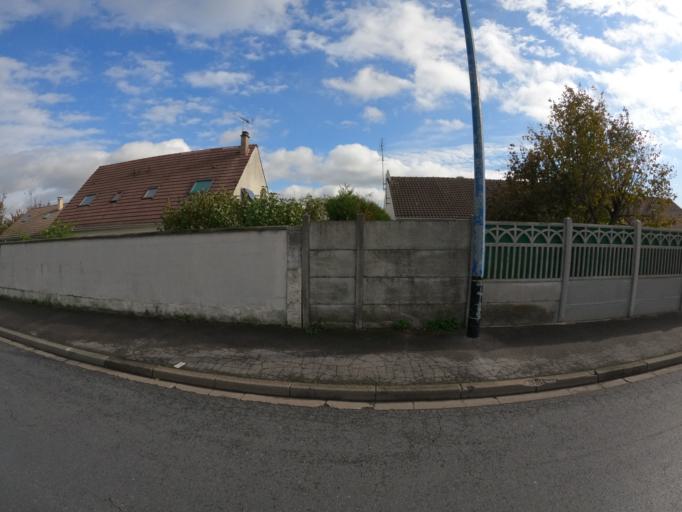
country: FR
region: Ile-de-France
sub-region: Departement de Seine-et-Marne
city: Chelles
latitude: 48.8910
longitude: 2.6036
